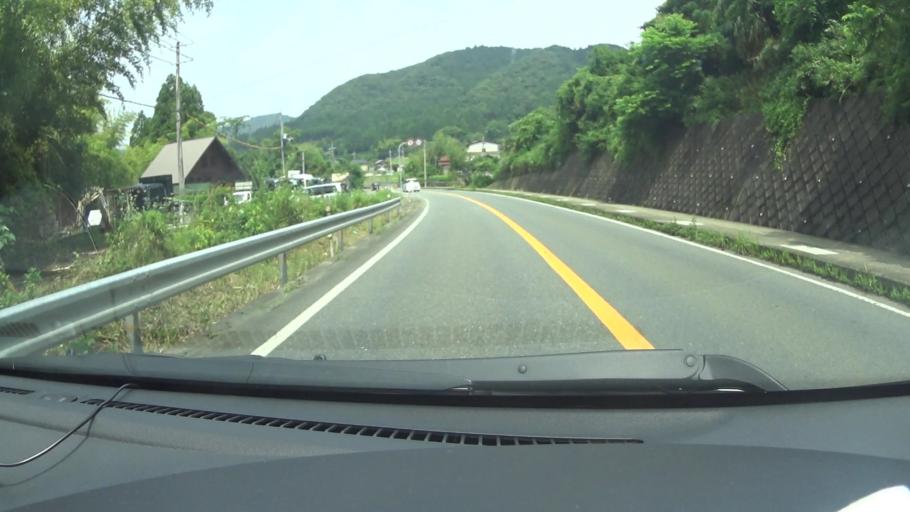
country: JP
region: Kyoto
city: Ayabe
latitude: 35.2970
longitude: 135.3279
